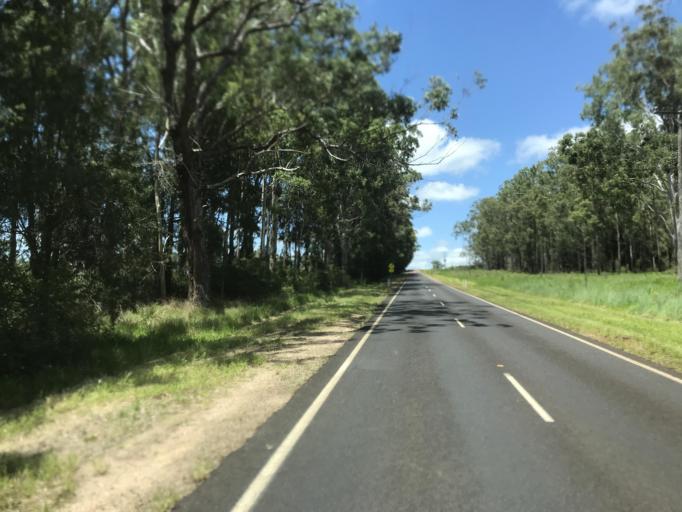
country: AU
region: Queensland
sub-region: Tablelands
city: Ravenshoe
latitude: -17.5341
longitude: 145.4526
